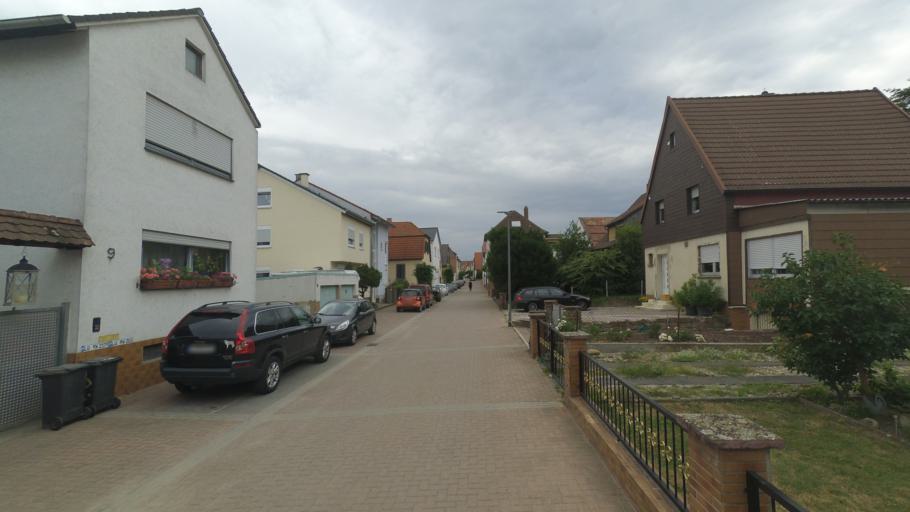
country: DE
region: Rheinland-Pfalz
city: Neuhofen
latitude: 49.4419
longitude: 8.4161
